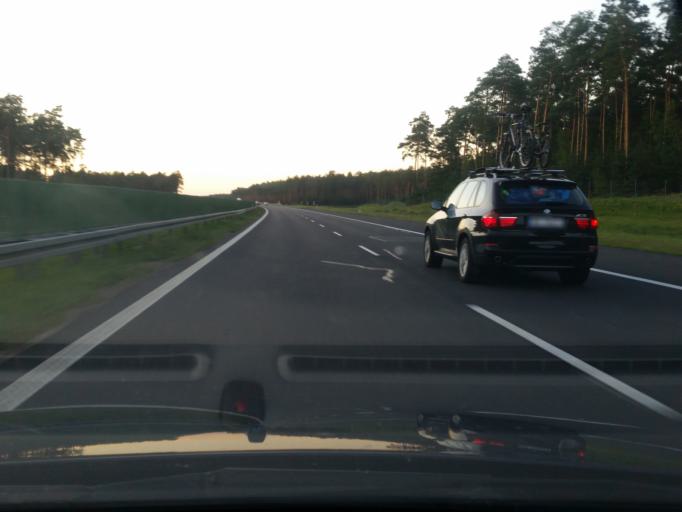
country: PL
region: Kujawsko-Pomorskie
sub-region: Powiat swiecki
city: Warlubie
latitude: 53.4943
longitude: 18.6150
